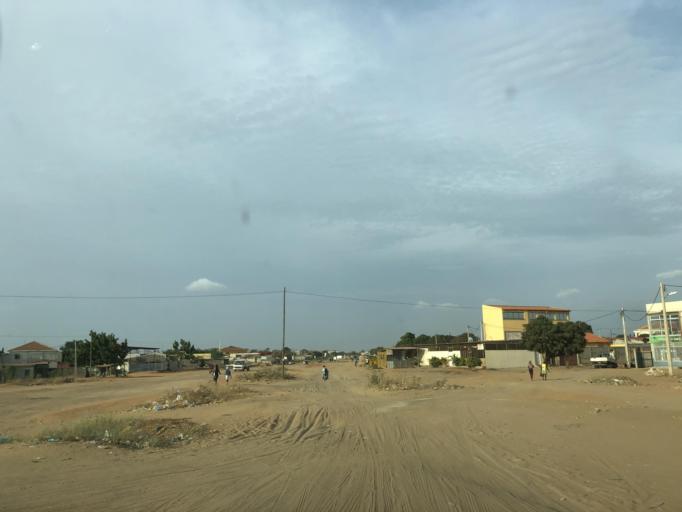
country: AO
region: Luanda
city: Luanda
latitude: -8.9211
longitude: 13.3083
